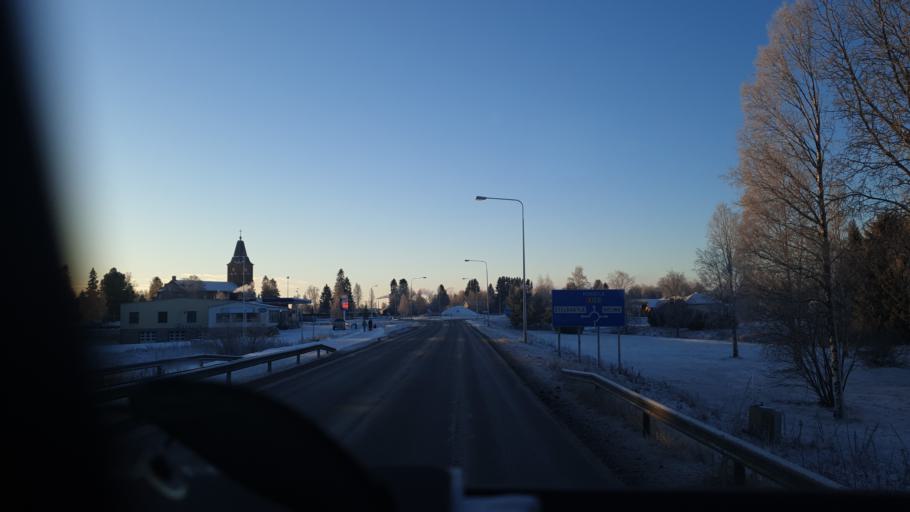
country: FI
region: Northern Ostrobothnia
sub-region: Ylivieska
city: Kalajoki
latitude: 64.2572
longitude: 23.9402
